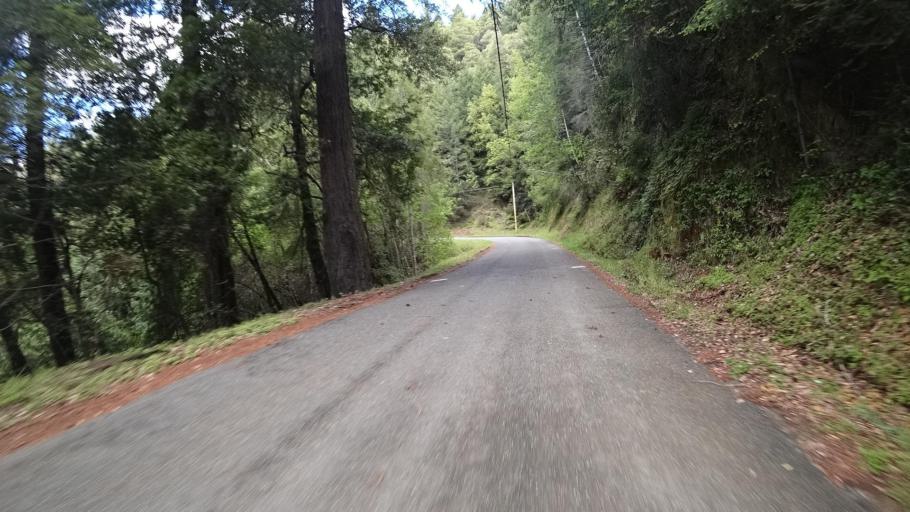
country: US
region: California
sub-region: Humboldt County
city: Blue Lake
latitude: 40.7626
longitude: -123.9258
